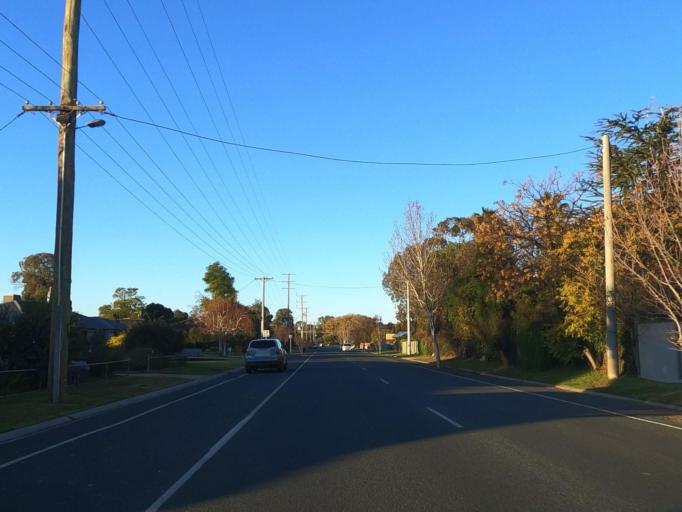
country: AU
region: Victoria
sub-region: Swan Hill
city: Swan Hill
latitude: -35.3599
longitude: 143.5581
